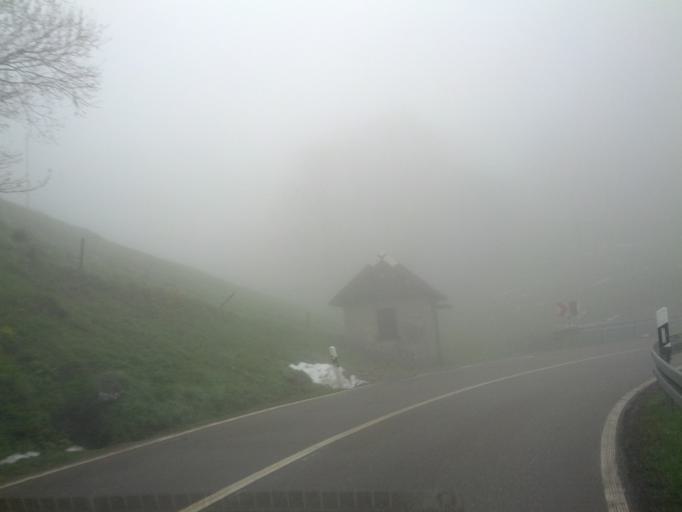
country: DE
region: Baden-Wuerttemberg
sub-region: Freiburg Region
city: Wieden
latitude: 47.8520
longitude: 7.8659
